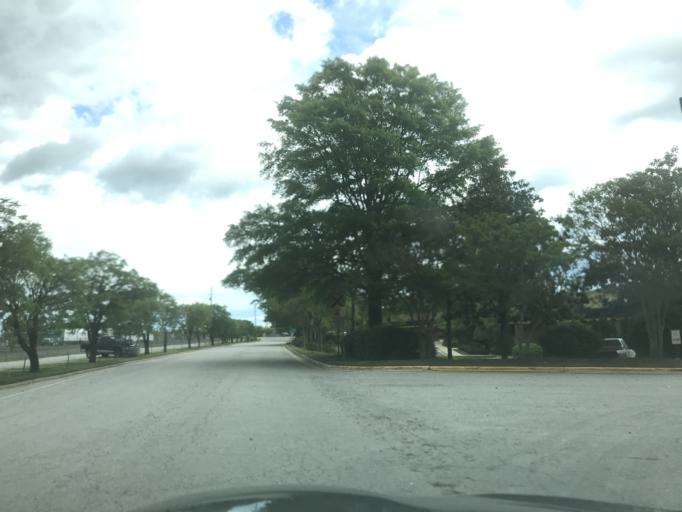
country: US
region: North Carolina
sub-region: Wake County
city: West Raleigh
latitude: 35.7930
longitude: -78.7083
